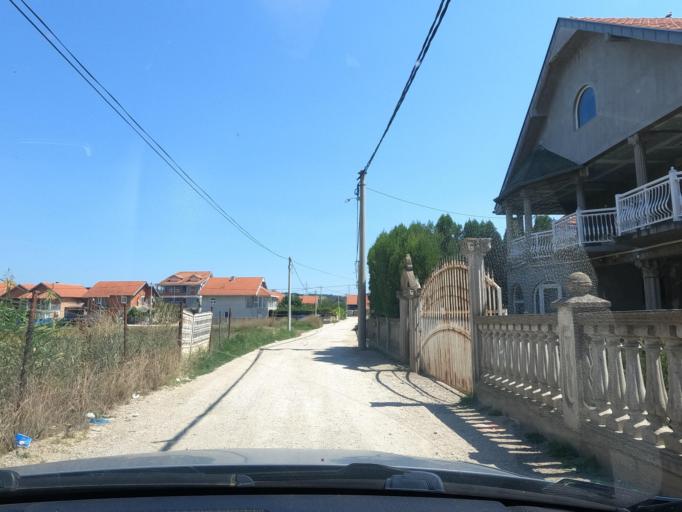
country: RS
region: Central Serbia
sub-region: Branicevski Okrug
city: Pozarevac
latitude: 44.7039
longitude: 21.1662
